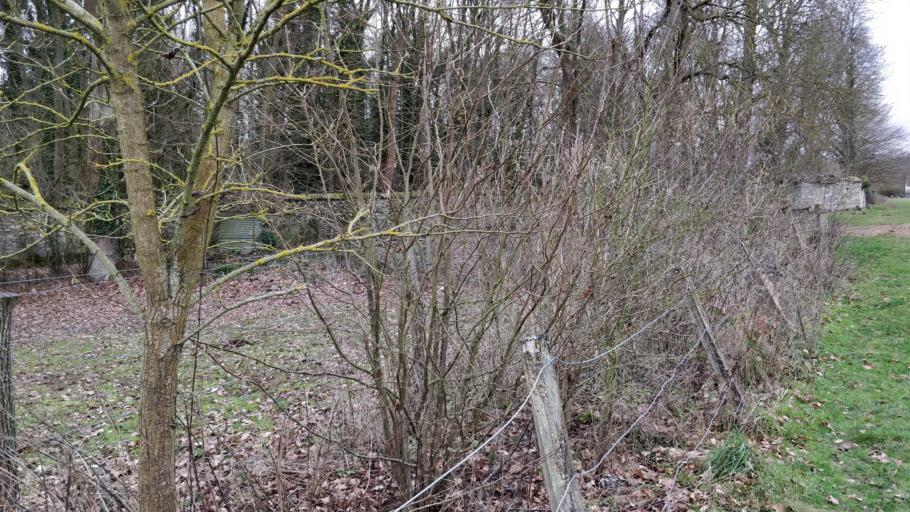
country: FR
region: Ile-de-France
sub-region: Departement de l'Essonne
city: Moigny-sur-Ecole
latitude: 48.4418
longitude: 2.4625
